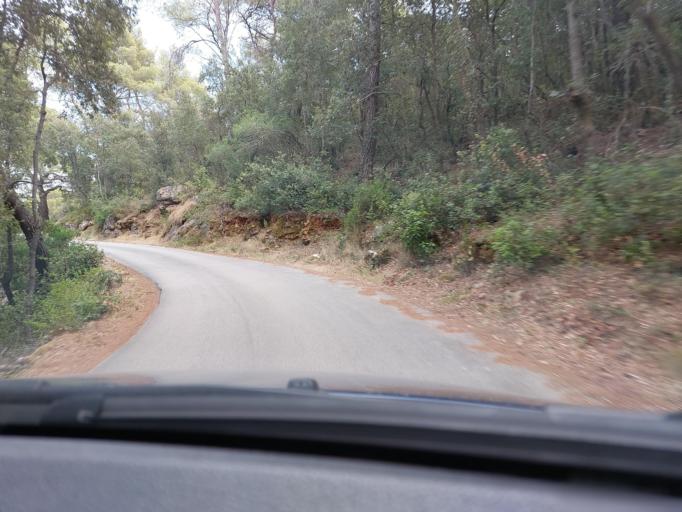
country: HR
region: Dubrovacko-Neretvanska
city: Smokvica
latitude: 42.7618
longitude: 16.9097
